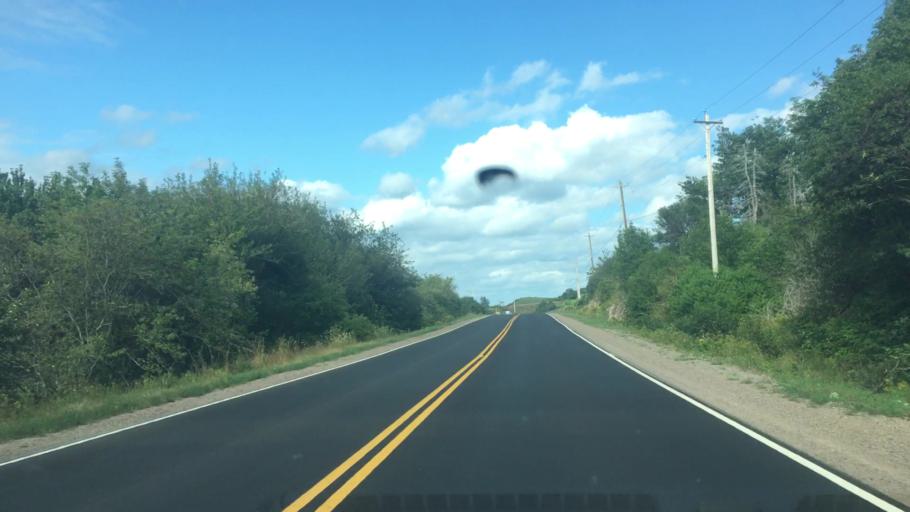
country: CA
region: Nova Scotia
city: Princeville
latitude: 45.7964
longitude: -60.7351
